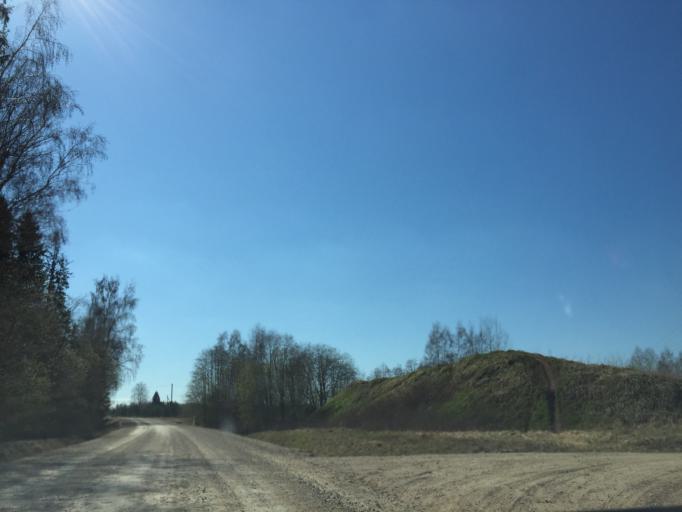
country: EE
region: Viljandimaa
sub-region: Viiratsi vald
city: Viiratsi
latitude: 58.3106
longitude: 25.6528
